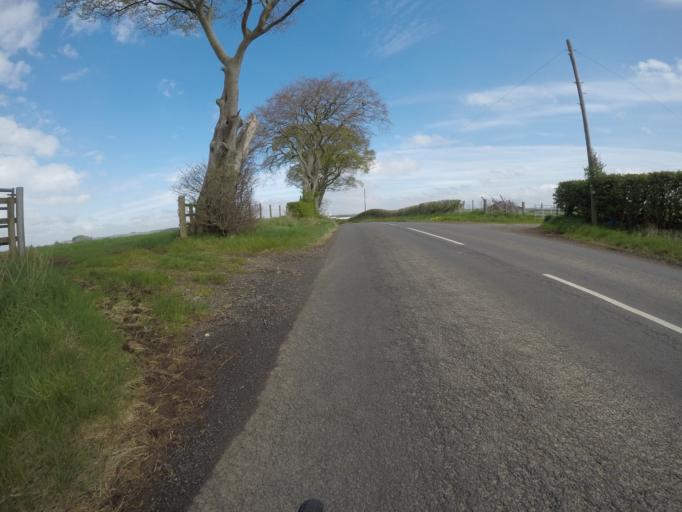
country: GB
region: Scotland
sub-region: East Ayrshire
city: Kilmaurs
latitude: 55.6531
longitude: -4.5630
